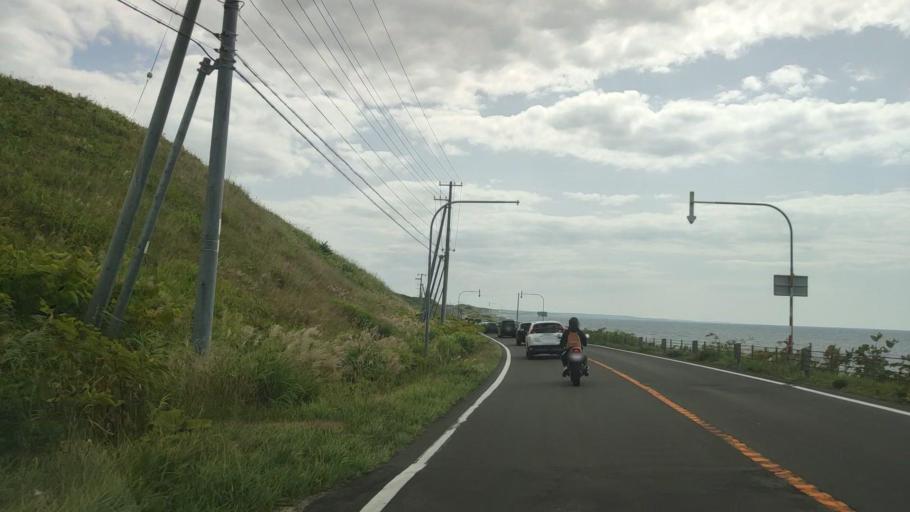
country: JP
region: Hokkaido
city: Rumoi
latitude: 44.5091
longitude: 141.7648
